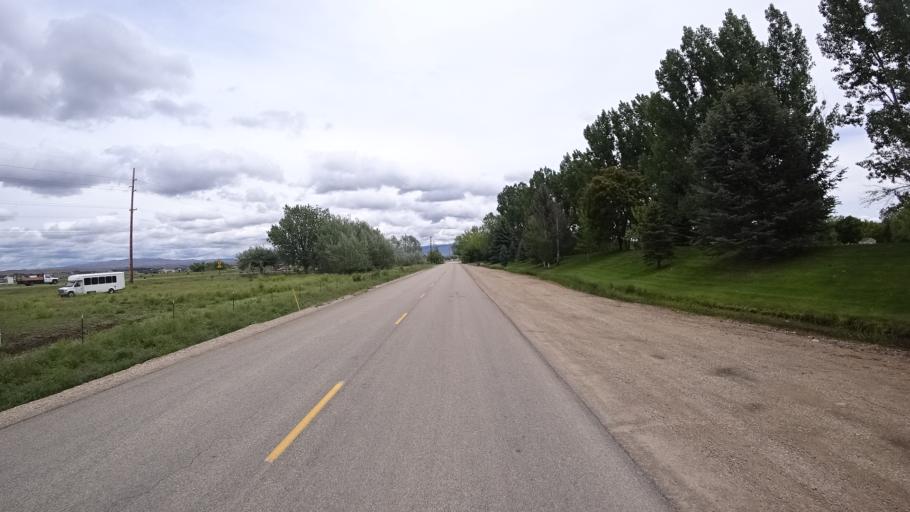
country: US
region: Idaho
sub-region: Ada County
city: Star
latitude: 43.6909
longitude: -116.4299
